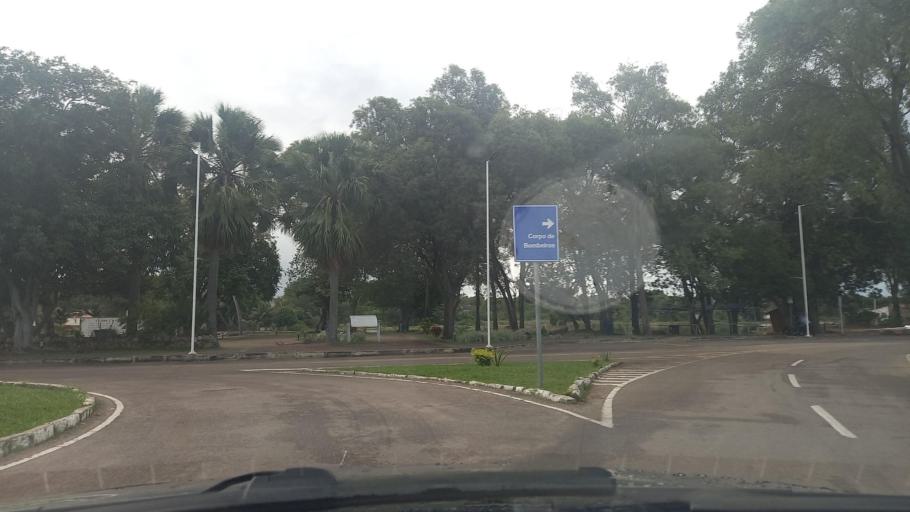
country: BR
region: Bahia
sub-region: Paulo Afonso
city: Paulo Afonso
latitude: -9.3963
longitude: -38.2120
